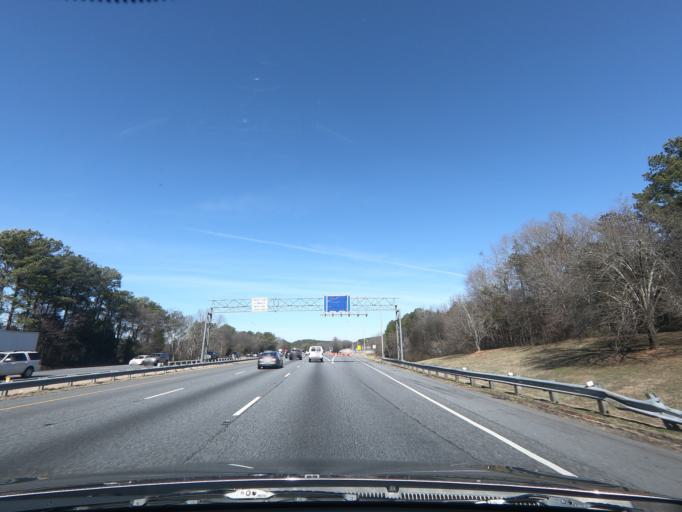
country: US
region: Georgia
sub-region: Bartow County
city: Adairsville
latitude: 34.4043
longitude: -84.9190
